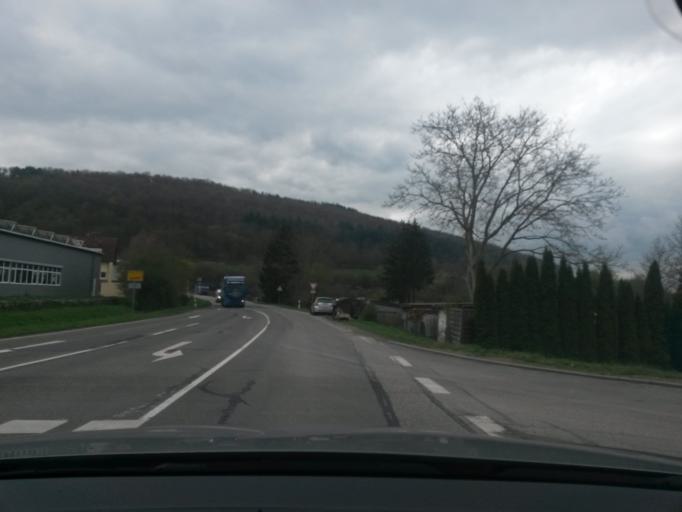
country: DE
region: Baden-Wuerttemberg
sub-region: Karlsruhe Region
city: Konigsbach-Stein
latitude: 48.9653
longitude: 8.6002
